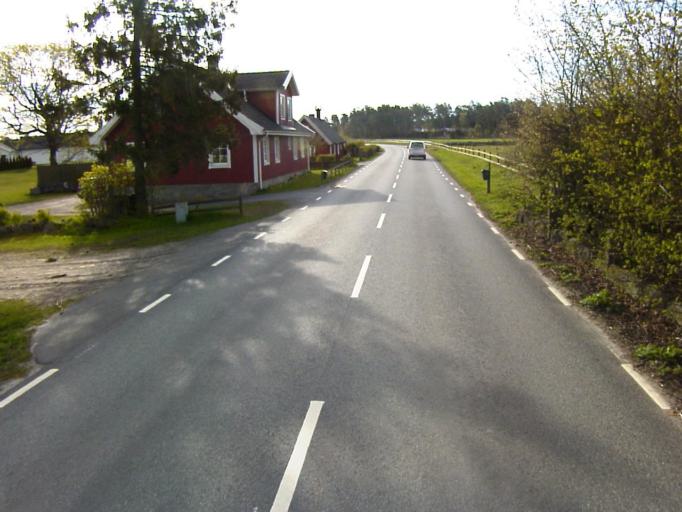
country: SE
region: Skane
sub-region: Kristianstads Kommun
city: Norra Asum
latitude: 55.9919
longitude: 14.1324
